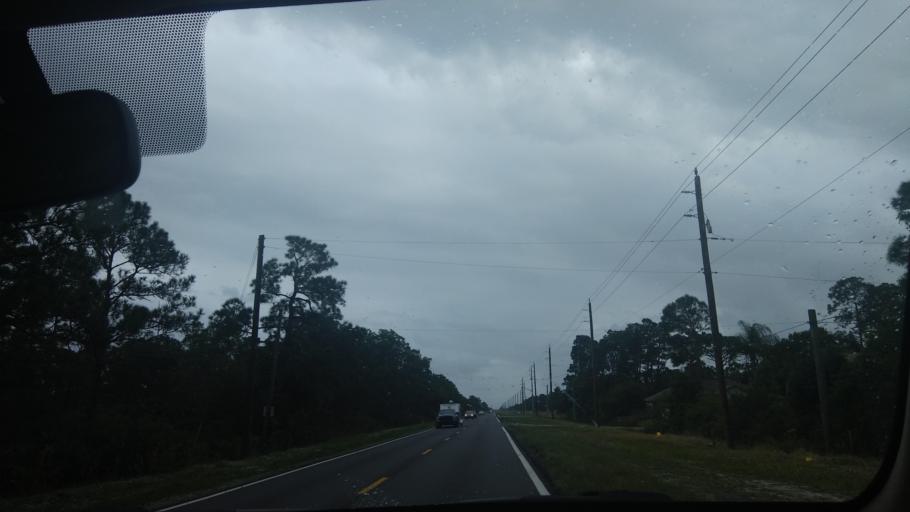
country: US
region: Florida
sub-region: Brevard County
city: Grant-Valkaria
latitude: 27.9406
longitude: -80.6228
